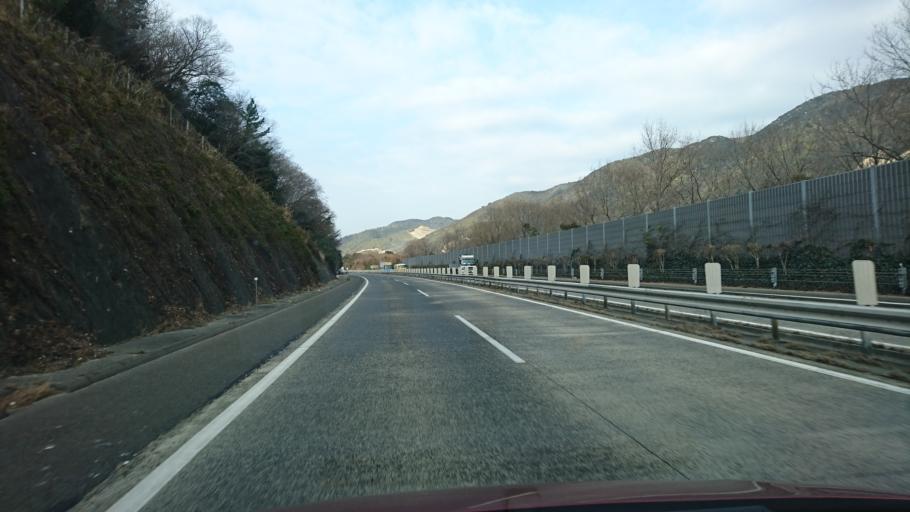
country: JP
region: Hyogo
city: Kariya
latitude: 34.7761
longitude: 134.3557
